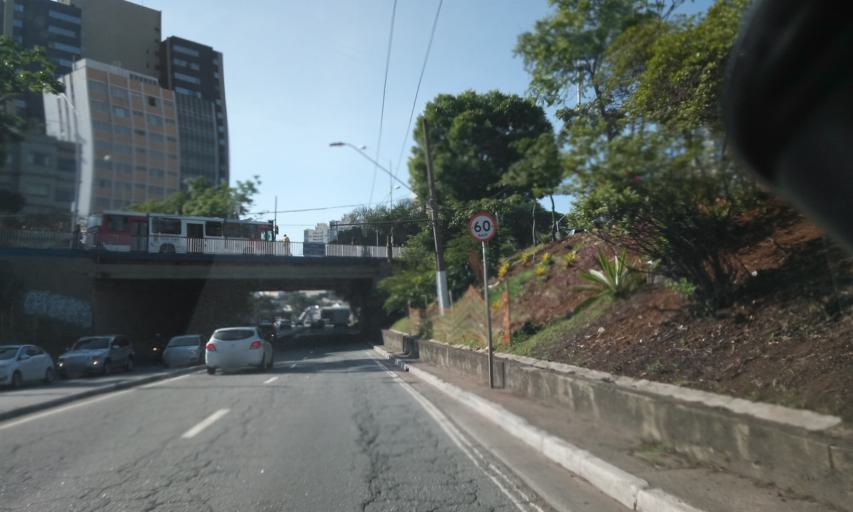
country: BR
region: Sao Paulo
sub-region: Santo Andre
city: Santo Andre
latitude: -23.6573
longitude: -46.5311
